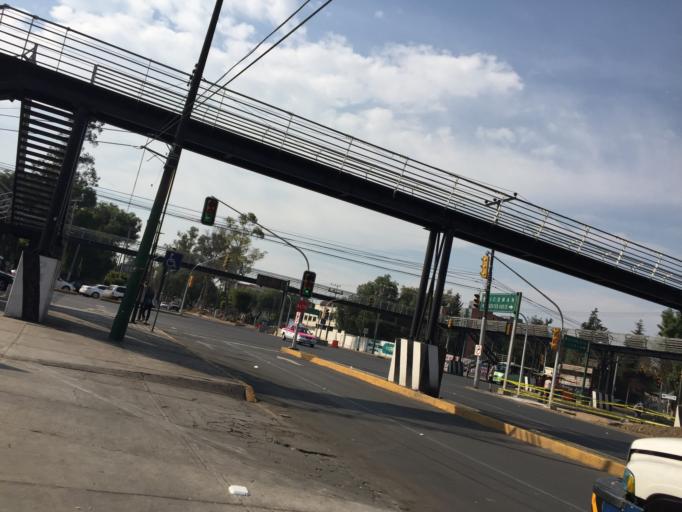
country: MX
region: Mexico
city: Colonia Lindavista
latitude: 19.5026
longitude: -99.1308
